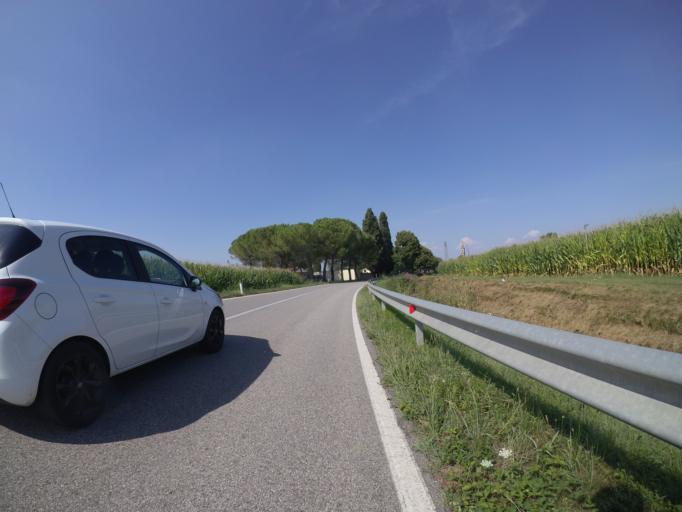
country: IT
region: Friuli Venezia Giulia
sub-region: Provincia di Udine
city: Lestizza
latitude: 45.9509
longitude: 13.1374
